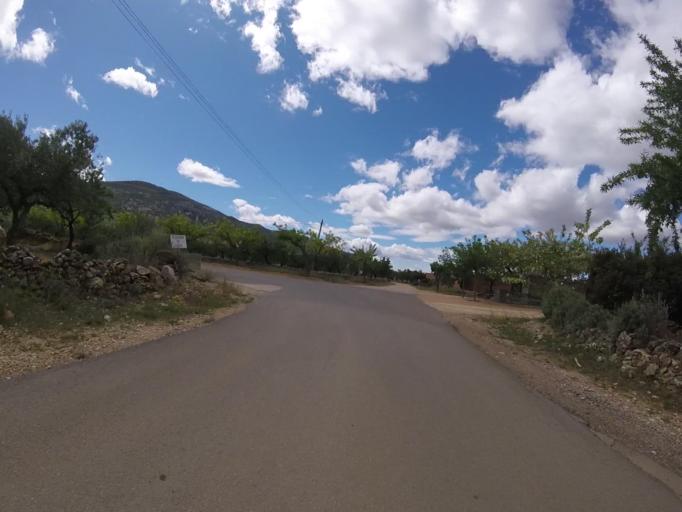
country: ES
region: Valencia
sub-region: Provincia de Castello
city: Sierra-Engarceran
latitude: 40.2906
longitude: -0.0558
